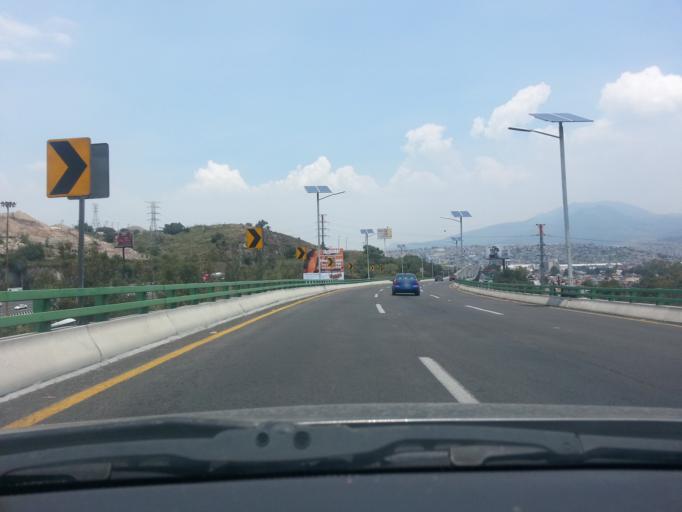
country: MX
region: Mexico
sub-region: Tultitlan
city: Buenavista
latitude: 19.5971
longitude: -99.1995
